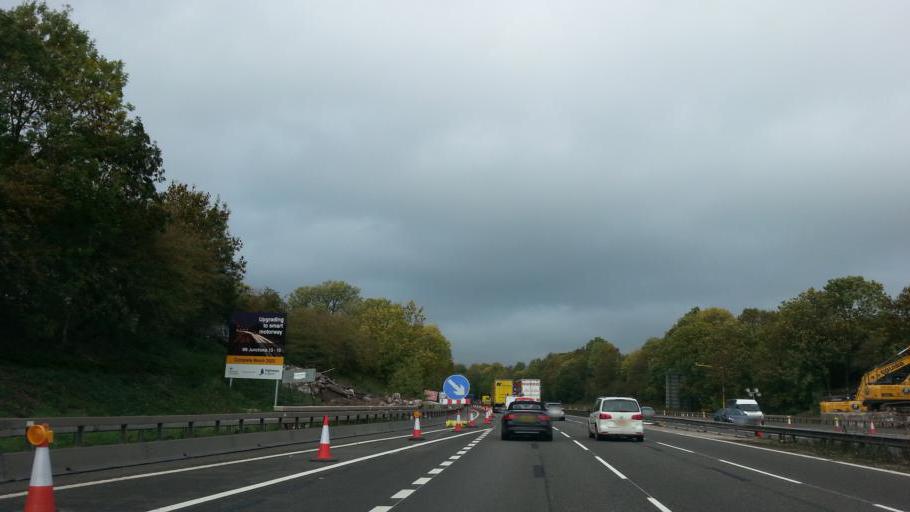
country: GB
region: England
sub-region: Staffordshire
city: Stafford
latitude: 52.8308
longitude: -2.1446
